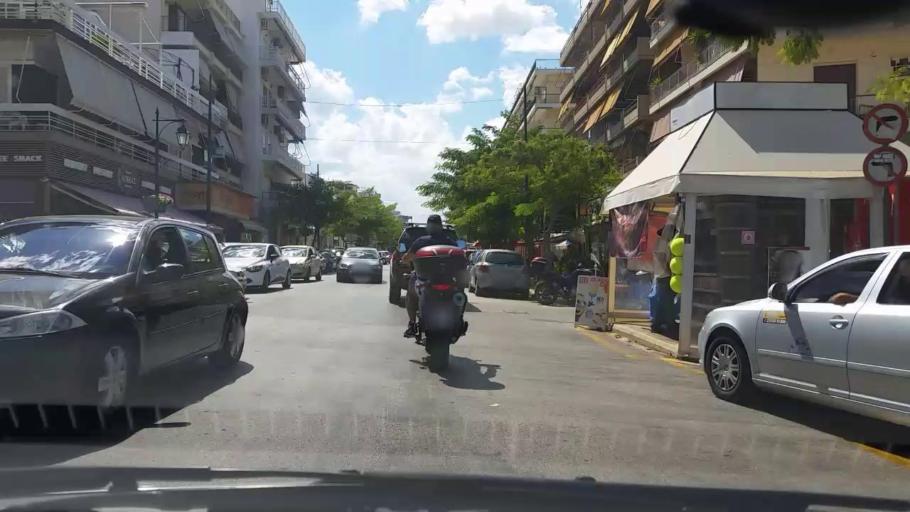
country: GR
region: Peloponnese
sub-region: Nomos Korinthias
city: Loutraki
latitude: 37.9735
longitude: 22.9777
